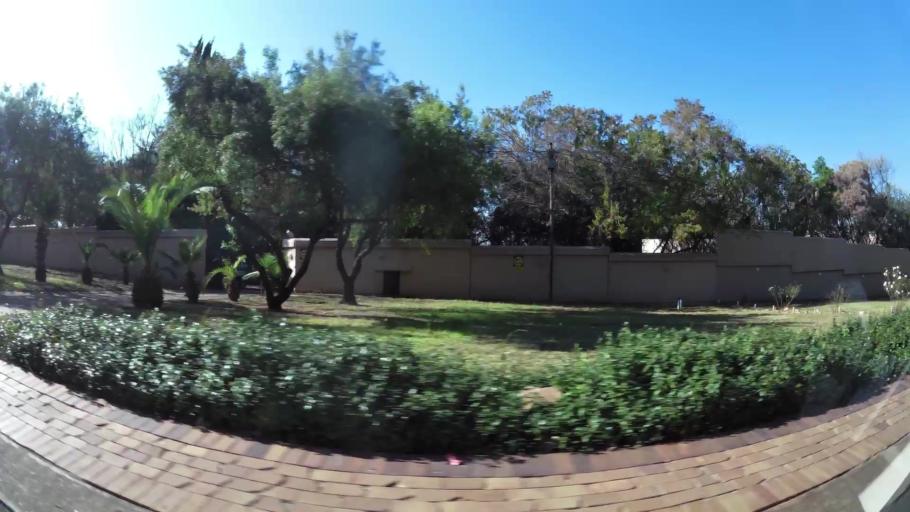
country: ZA
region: Gauteng
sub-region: City of Johannesburg Metropolitan Municipality
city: Midrand
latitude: -26.0575
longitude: 28.0314
